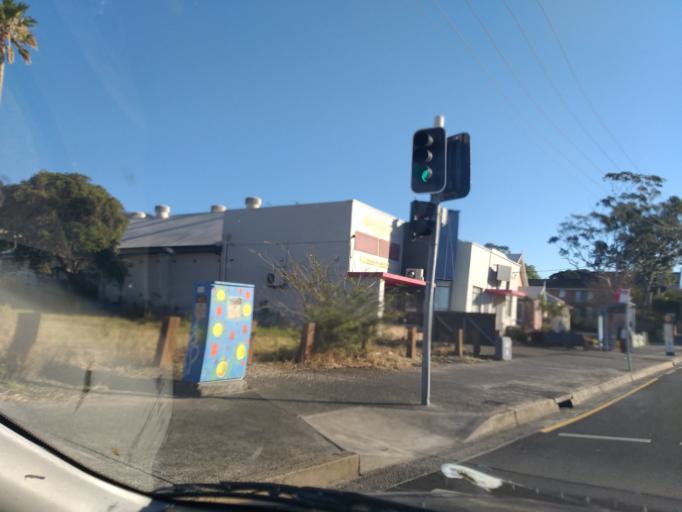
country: AU
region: New South Wales
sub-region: Wollongong
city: Corrimal
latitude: -34.3701
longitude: 150.8975
